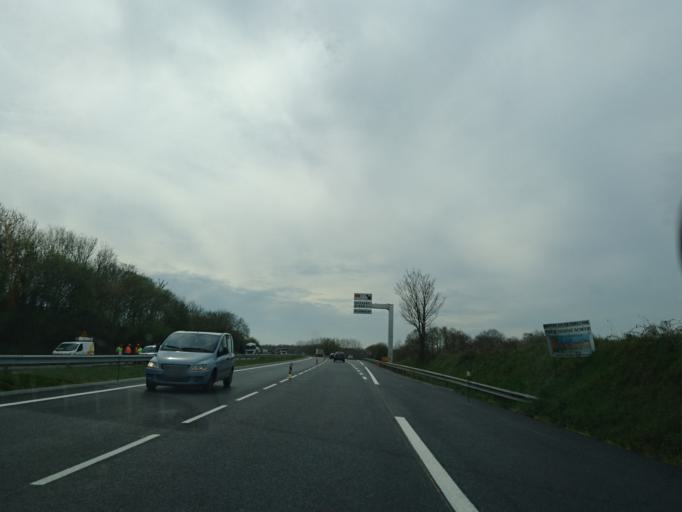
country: FR
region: Brittany
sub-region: Departement des Cotes-d'Armor
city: Lehon
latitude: 48.4709
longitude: -2.0556
